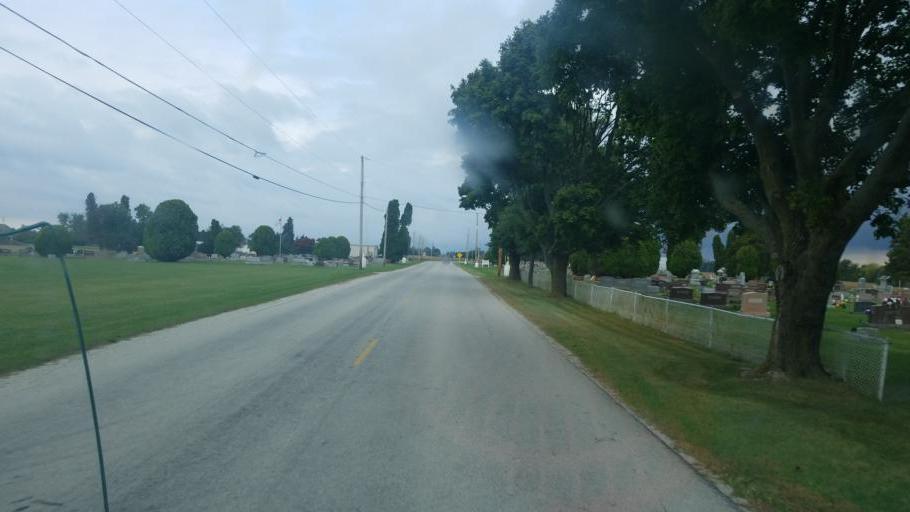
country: US
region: Ohio
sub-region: Wood County
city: North Baltimore
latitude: 41.1837
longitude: -83.6086
